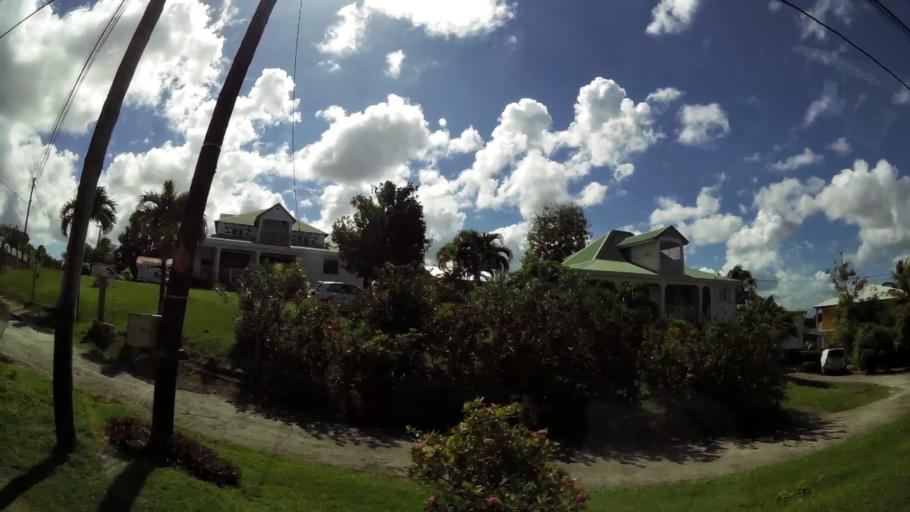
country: GP
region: Guadeloupe
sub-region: Guadeloupe
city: Petit-Canal
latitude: 16.3502
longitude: -61.4203
